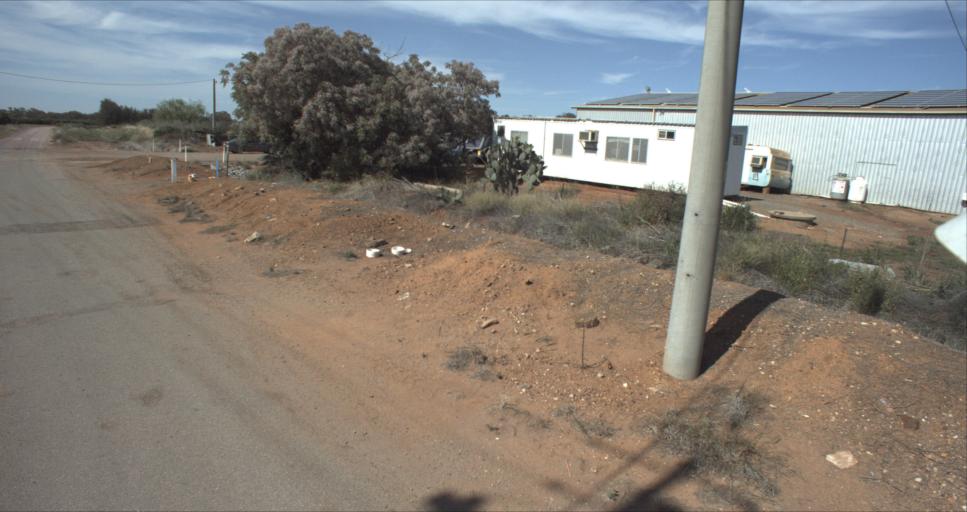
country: AU
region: New South Wales
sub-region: Leeton
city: Leeton
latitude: -34.5808
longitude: 146.4883
